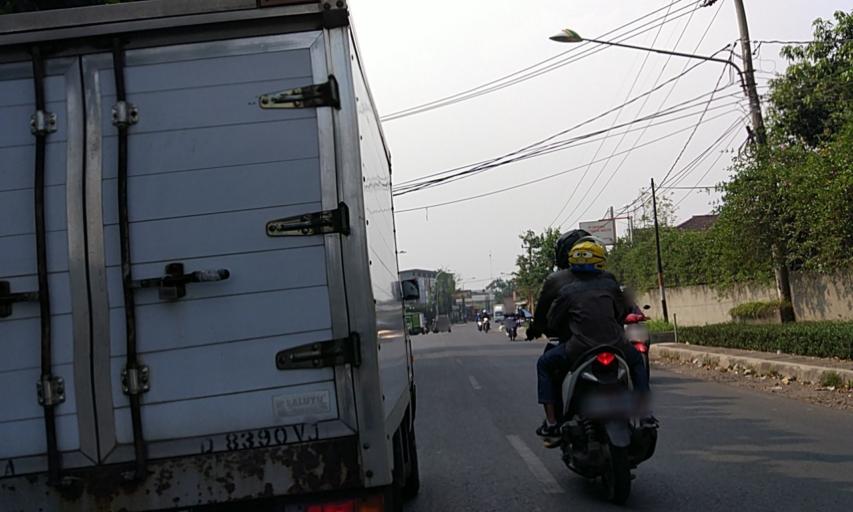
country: ID
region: West Java
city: Margahayukencana
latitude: -6.9909
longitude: 107.5564
